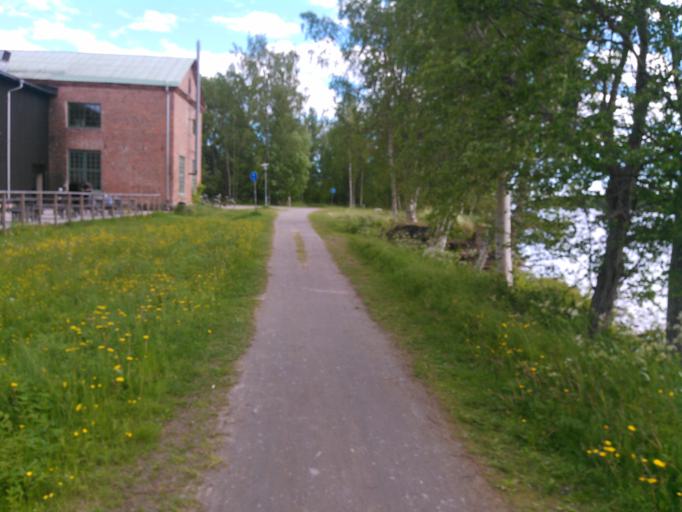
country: SE
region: Vaesterbotten
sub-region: Umea Kommun
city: Umea
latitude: 63.7937
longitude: 20.3044
